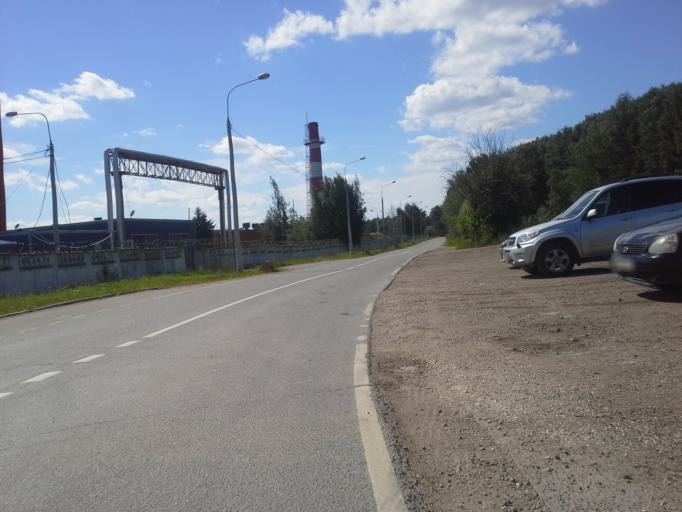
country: RU
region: Moscow
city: Solntsevo
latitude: 55.6590
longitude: 37.3772
